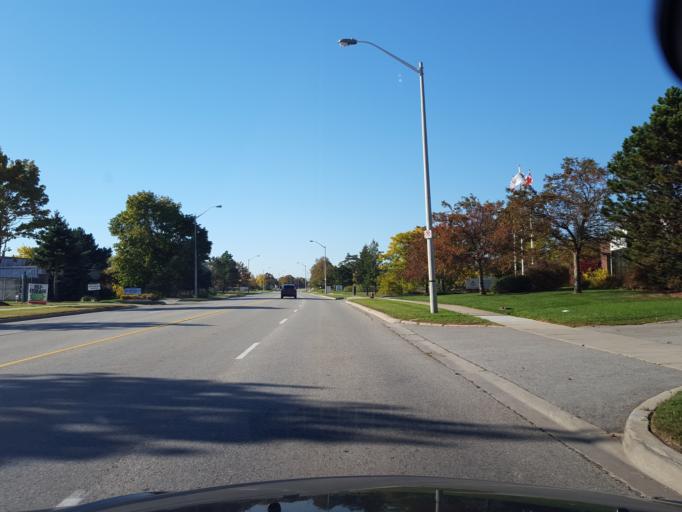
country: CA
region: Ontario
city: Burlington
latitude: 43.3707
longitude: -79.7970
